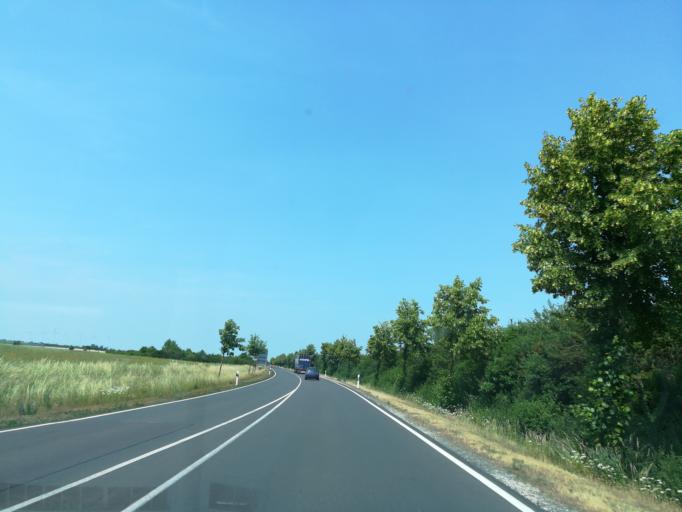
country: DE
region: Saxony-Anhalt
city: Egeln
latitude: 51.9308
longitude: 11.4195
